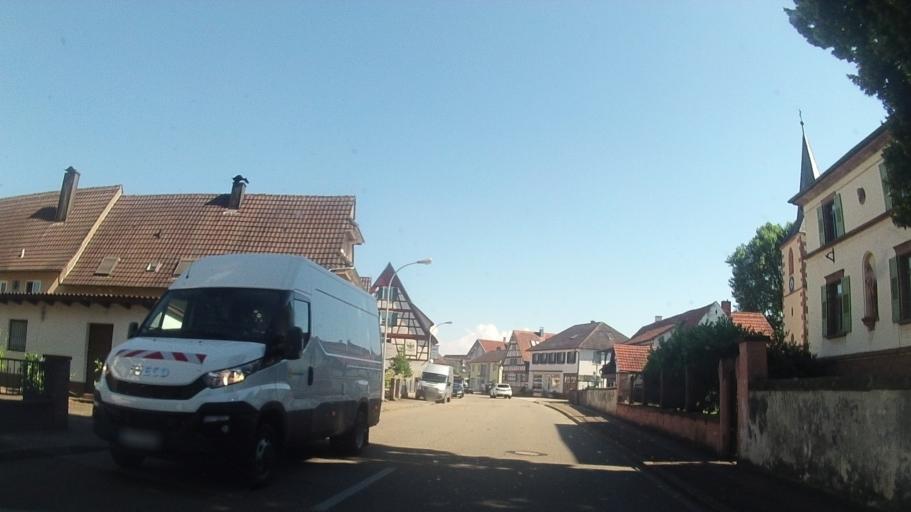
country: DE
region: Baden-Wuerttemberg
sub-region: Freiburg Region
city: Offenburg
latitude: 48.5097
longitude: 7.9243
